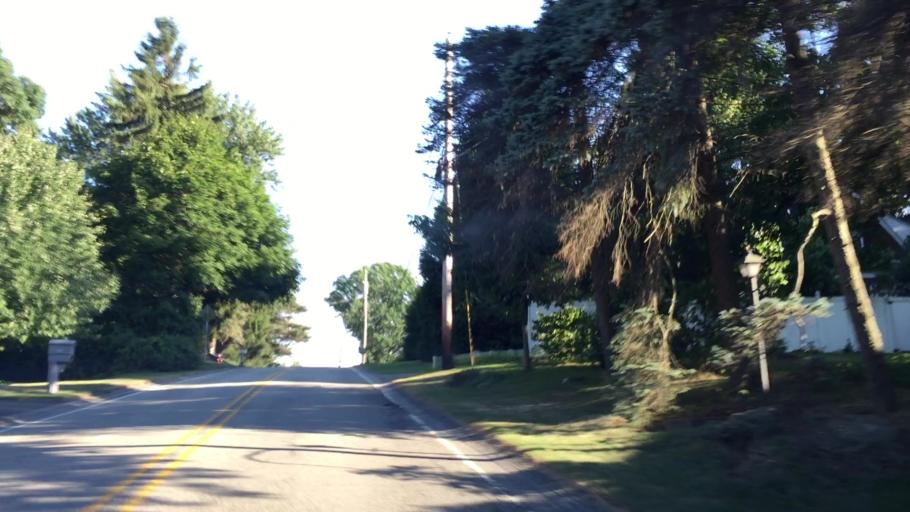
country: US
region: Pennsylvania
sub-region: Allegheny County
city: Franklin Park
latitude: 40.5869
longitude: -80.0548
